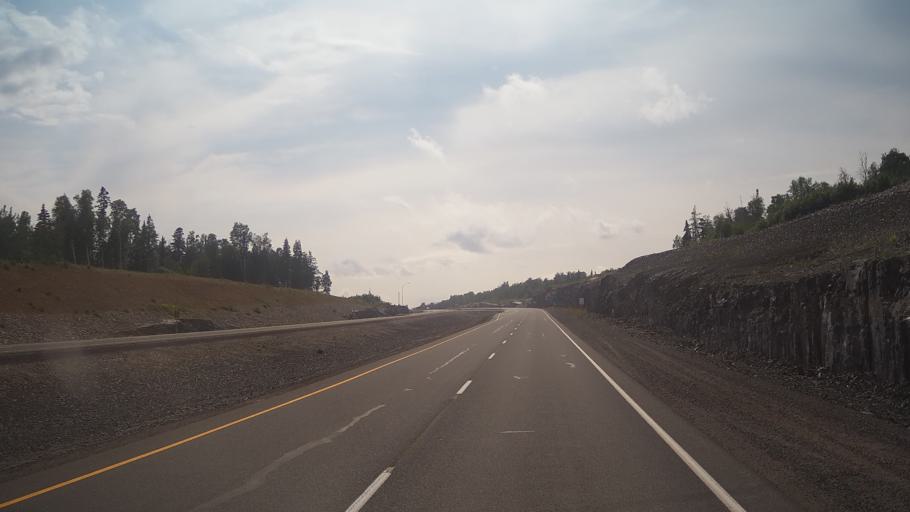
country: CA
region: Ontario
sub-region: Thunder Bay District
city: Thunder Bay
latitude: 48.5678
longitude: -88.8481
